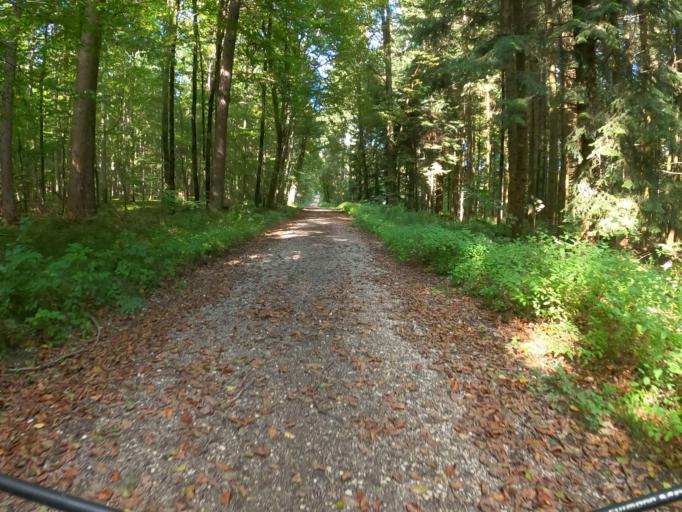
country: DE
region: Bavaria
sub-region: Swabia
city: Roggenburg
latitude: 48.3226
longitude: 10.2448
